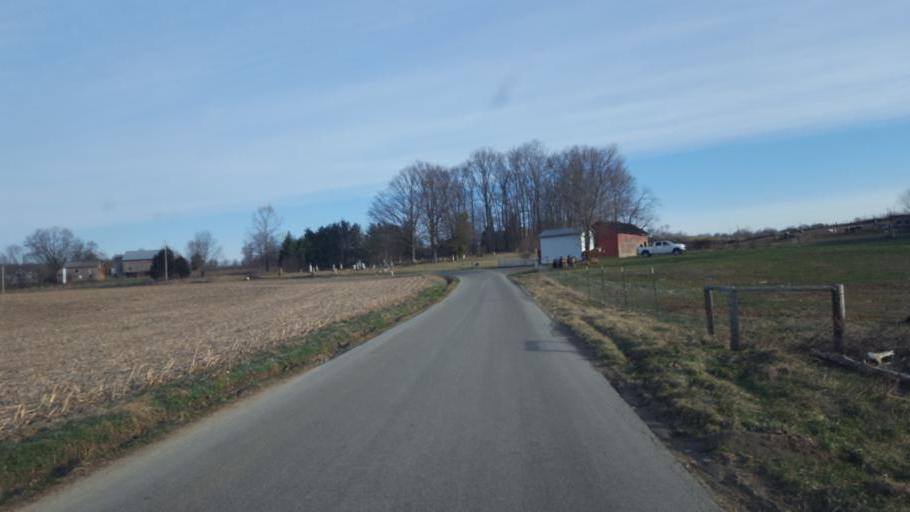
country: US
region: Ohio
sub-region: Knox County
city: Fredericktown
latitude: 40.5467
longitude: -82.6196
